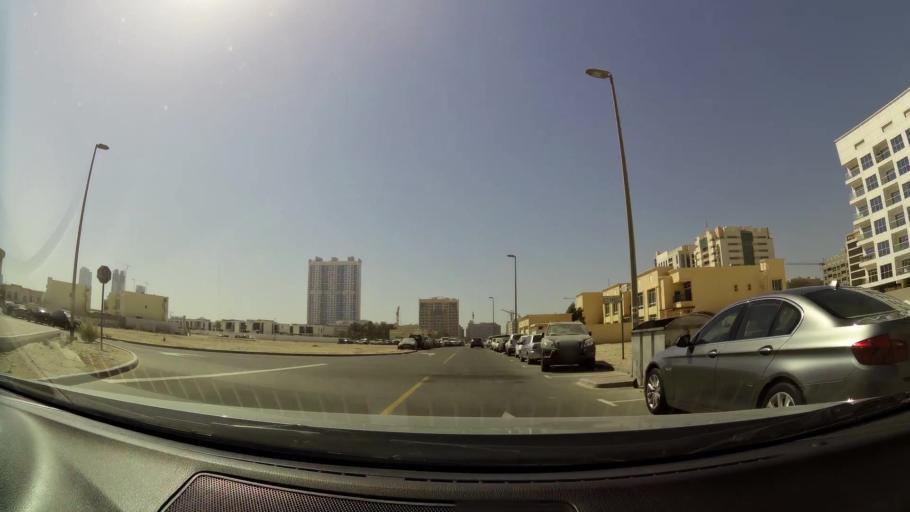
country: AE
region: Dubai
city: Dubai
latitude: 25.1074
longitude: 55.1966
